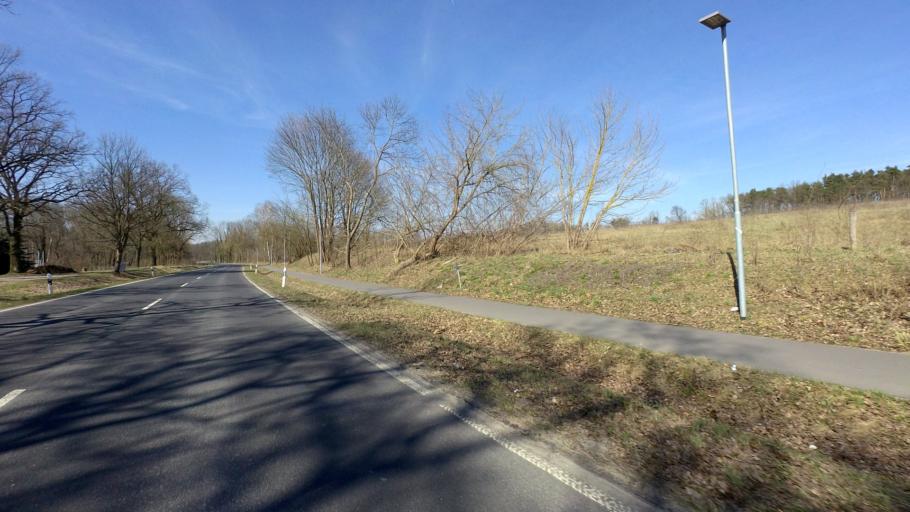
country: DE
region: Brandenburg
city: Muncheberg
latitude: 52.5190
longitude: 14.1091
